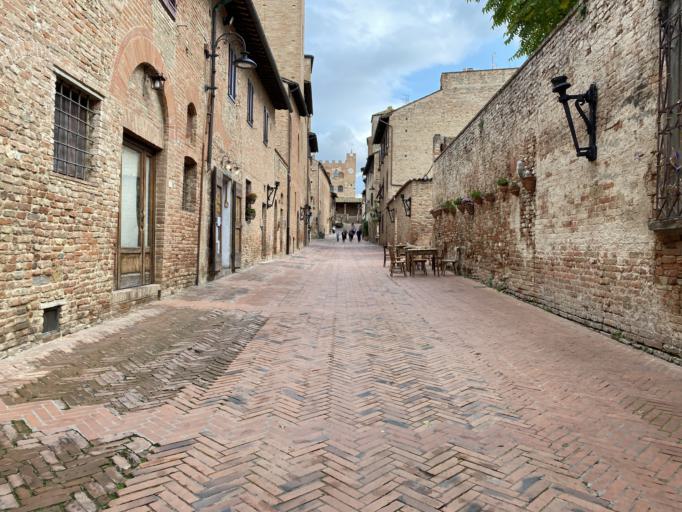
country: IT
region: Tuscany
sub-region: Province of Florence
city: Certaldo
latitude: 43.5489
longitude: 11.0439
